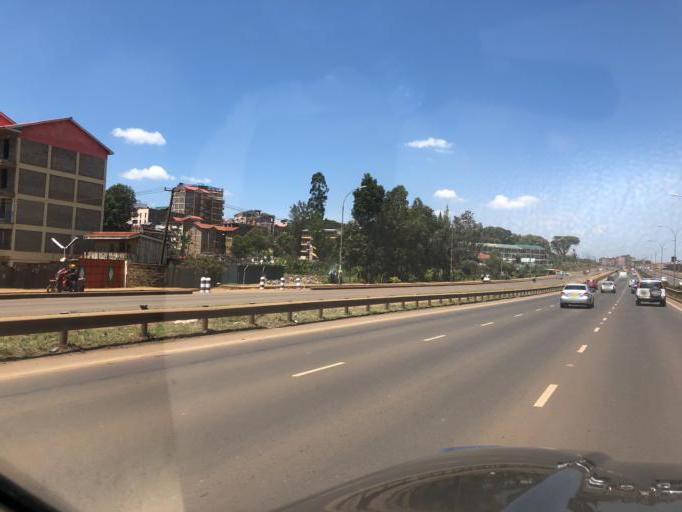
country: KE
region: Kiambu
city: Kiambu
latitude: -1.2115
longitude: 36.9059
